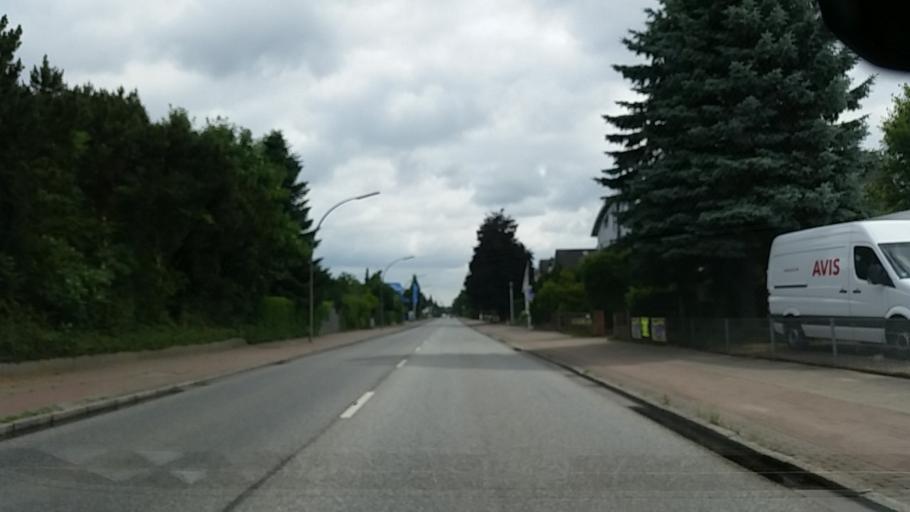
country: DE
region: Schleswig-Holstein
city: Norderstedt
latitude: 53.6706
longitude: 9.9820
